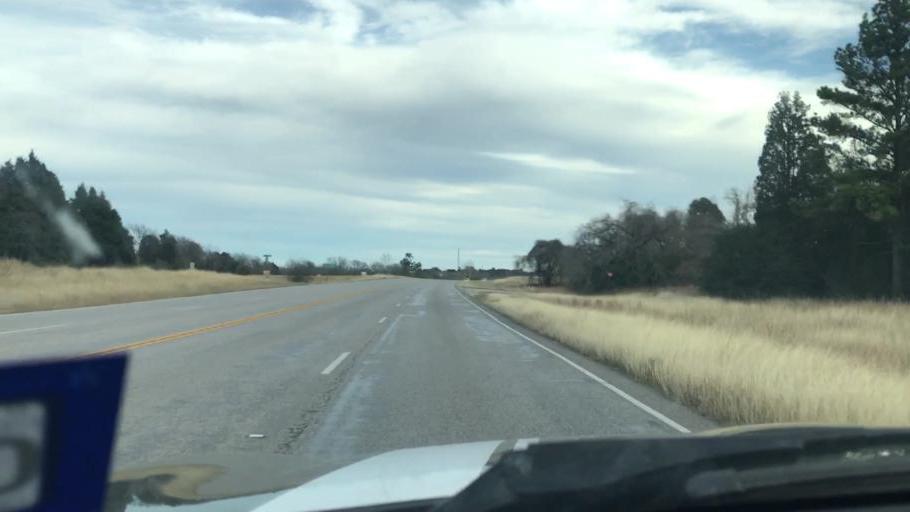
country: US
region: Texas
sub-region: Bastrop County
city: Camp Swift
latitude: 30.2966
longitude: -97.2710
